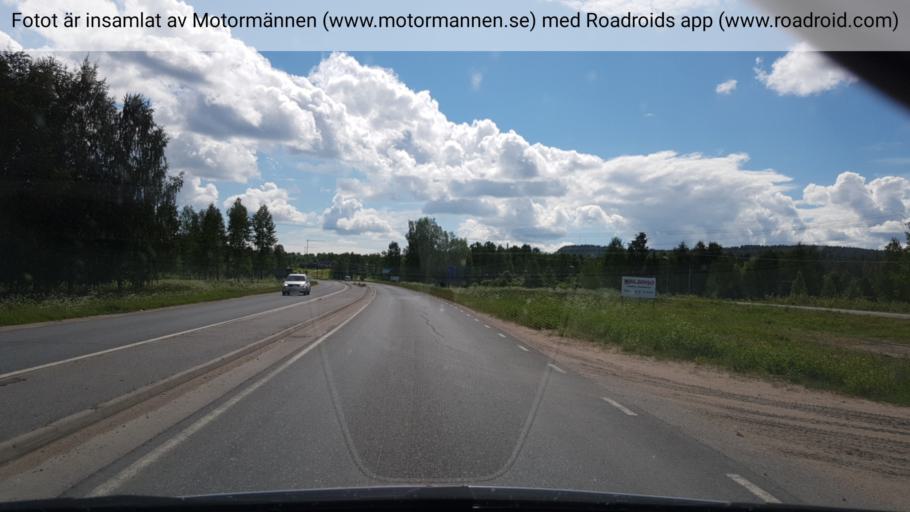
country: SE
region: Norrbotten
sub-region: Overtornea Kommun
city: OEvertornea
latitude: 66.3960
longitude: 23.6265
